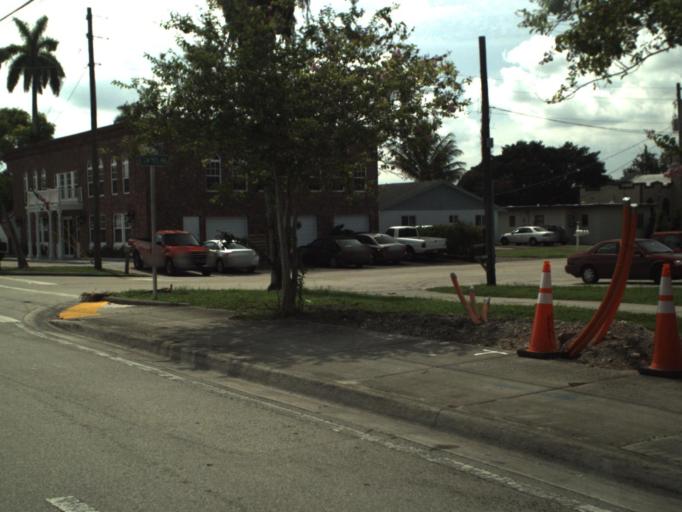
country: US
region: Florida
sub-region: Broward County
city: Davie
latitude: 26.0649
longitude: -80.2334
